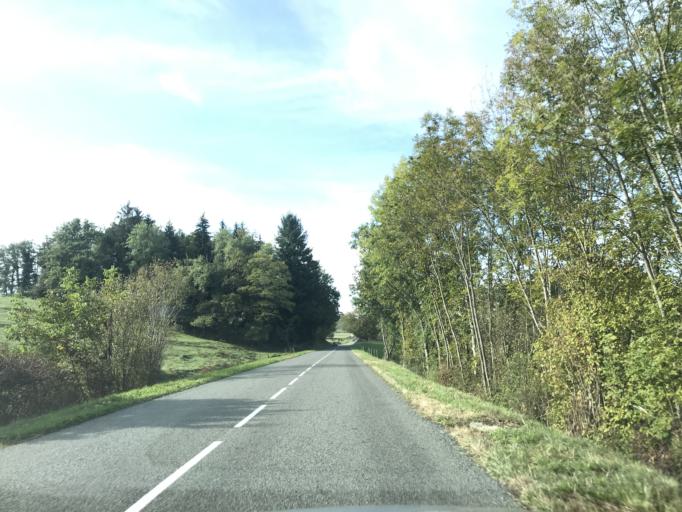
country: FR
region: Rhone-Alpes
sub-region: Departement de la Savoie
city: Yenne
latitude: 45.6841
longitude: 5.7955
